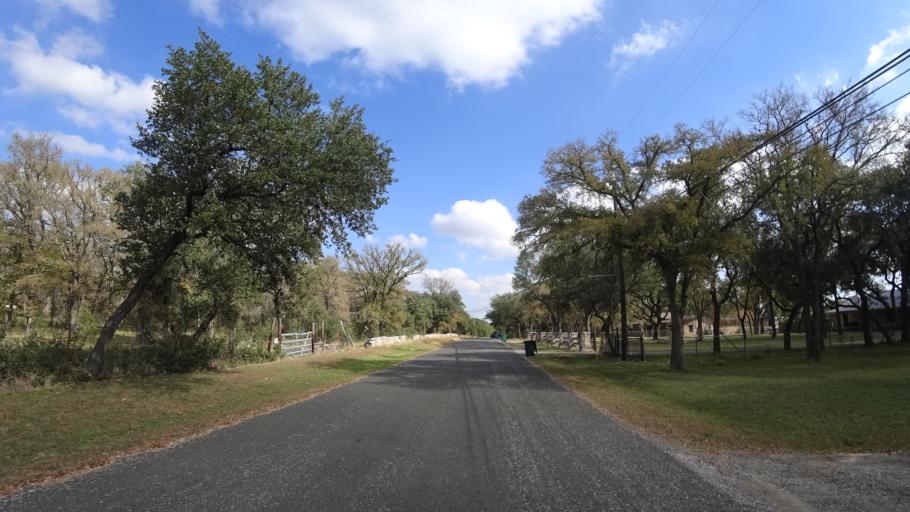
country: US
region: Texas
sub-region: Travis County
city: Shady Hollow
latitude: 30.1759
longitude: -97.8654
